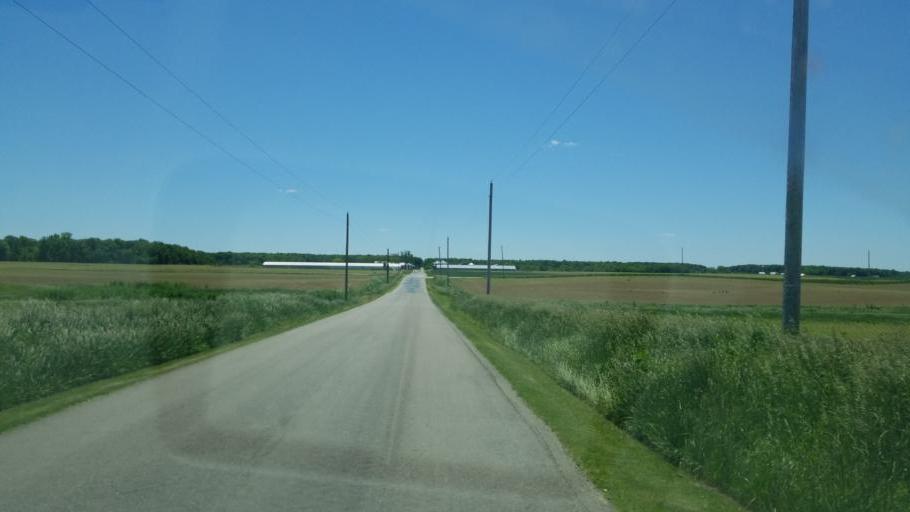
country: US
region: Ohio
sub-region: Mercer County
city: Fort Recovery
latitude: 40.3405
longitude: -84.8038
